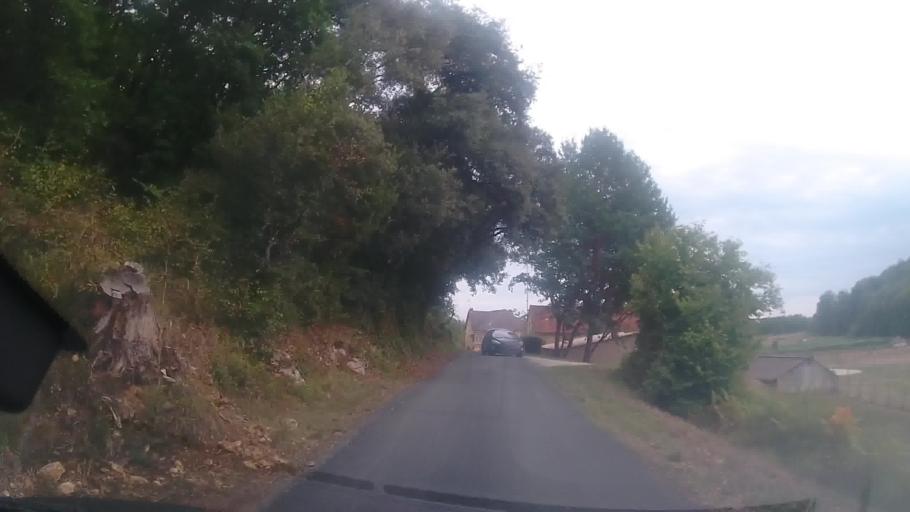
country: FR
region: Aquitaine
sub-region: Departement de la Dordogne
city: Eyvigues-et-Eybenes
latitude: 44.8389
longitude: 1.3543
